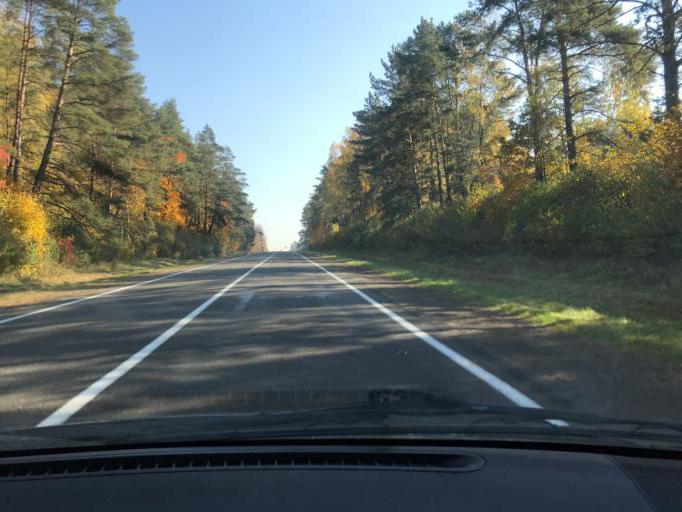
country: BY
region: Minsk
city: Klyetsk
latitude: 52.9689
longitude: 26.6147
